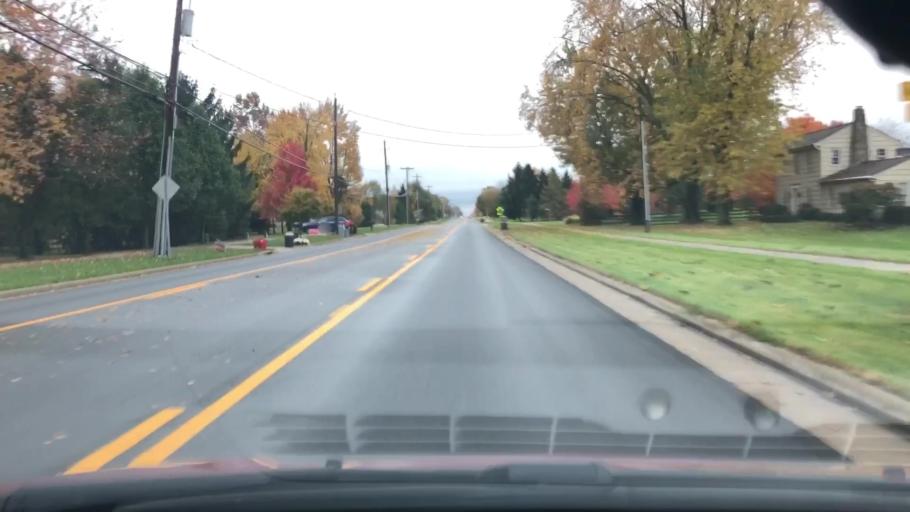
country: US
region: Ohio
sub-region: Franklin County
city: Westerville
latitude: 40.1668
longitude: -82.8996
